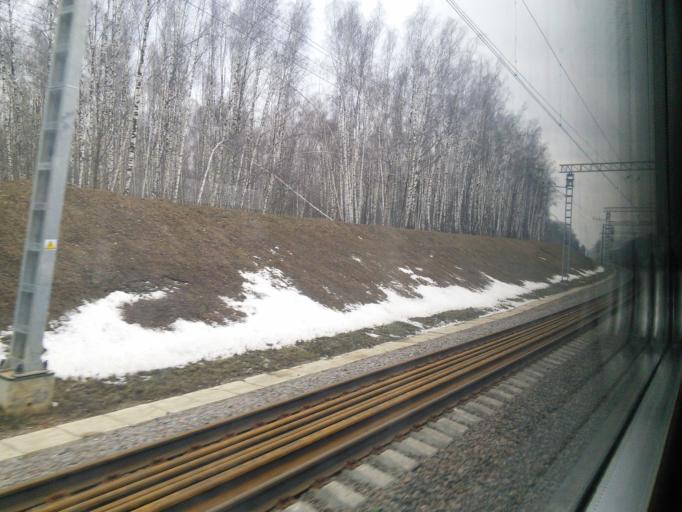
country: RU
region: Moskovskaya
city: Vostryakovo
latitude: 55.4345
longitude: 37.8531
